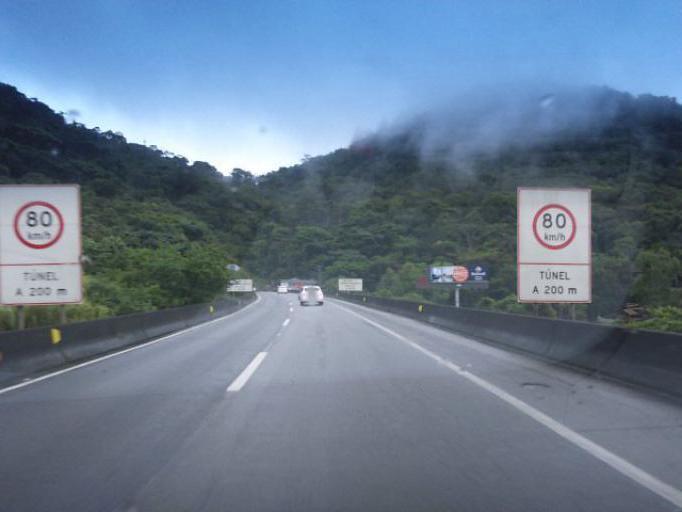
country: BR
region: Santa Catarina
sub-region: Itapema
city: Itapema
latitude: -27.0492
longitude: -48.5978
